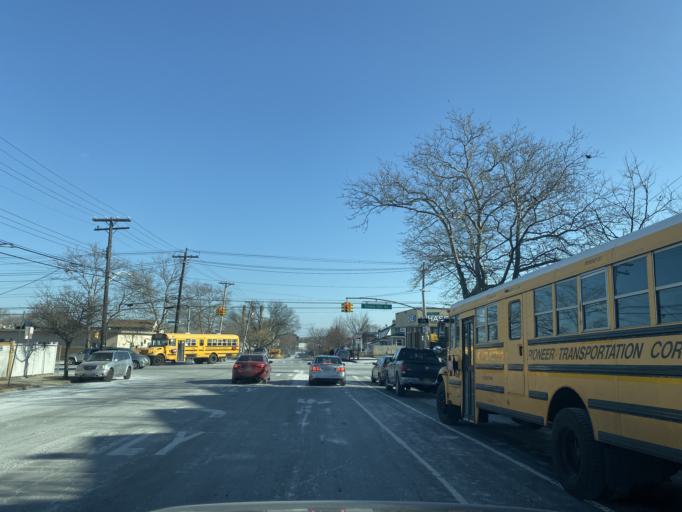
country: US
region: New York
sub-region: Bronx
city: The Bronx
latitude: 40.8232
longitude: -73.8496
